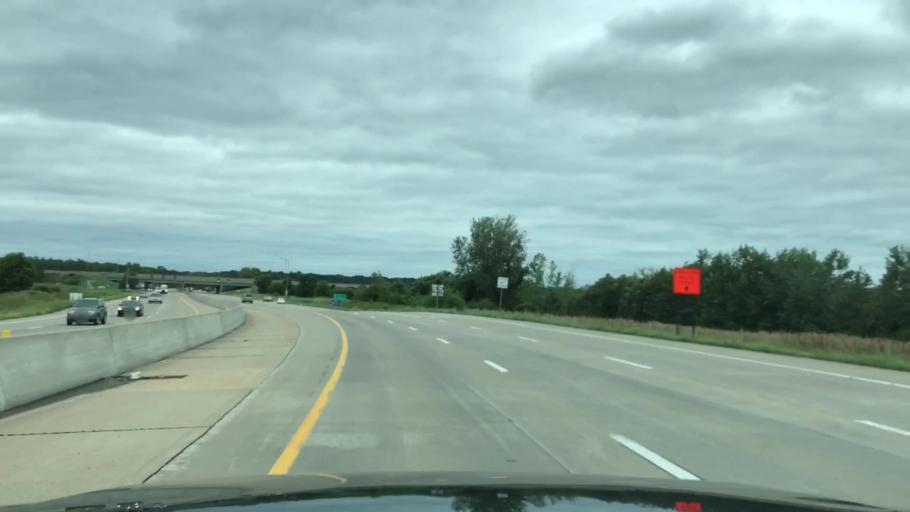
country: US
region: Missouri
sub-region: Saint Louis County
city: Maryland Heights
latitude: 38.7125
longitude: -90.5011
